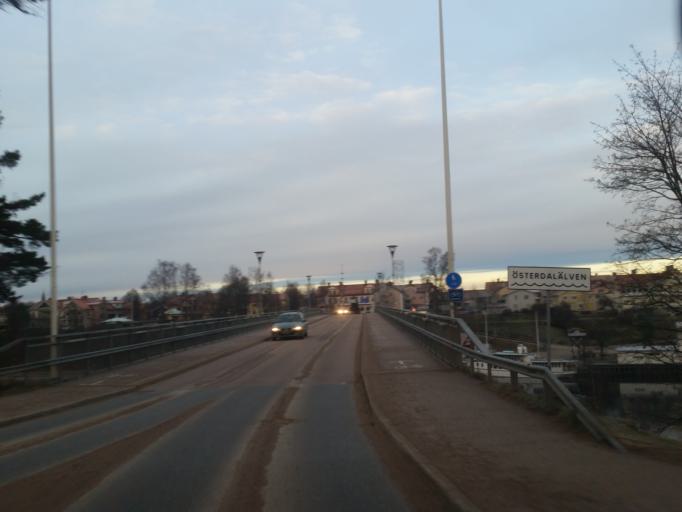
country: SE
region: Dalarna
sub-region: Leksand Municipality
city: Leksand
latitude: 60.7276
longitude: 14.9985
